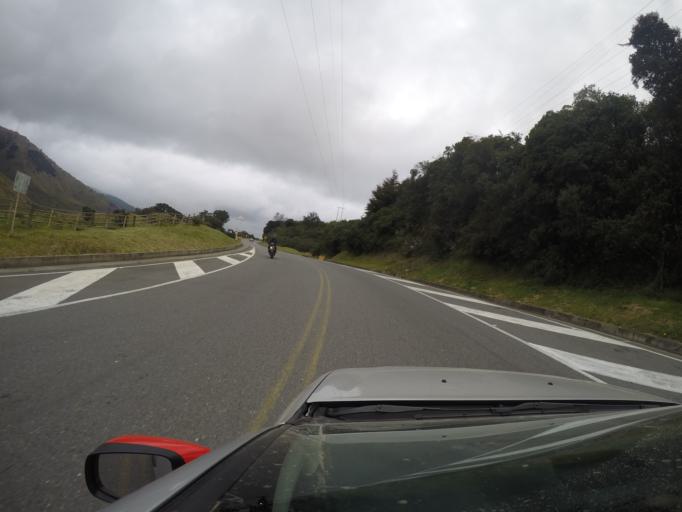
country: CO
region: Caldas
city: Villamaria
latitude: 5.0148
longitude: -75.3413
